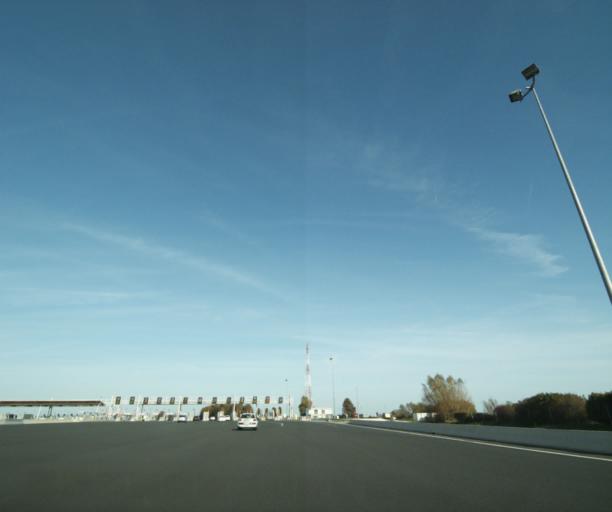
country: FR
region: Ile-de-France
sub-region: Departement de Seine-et-Marne
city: Bailly-Romainvilliers
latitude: 48.8523
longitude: 2.8376
